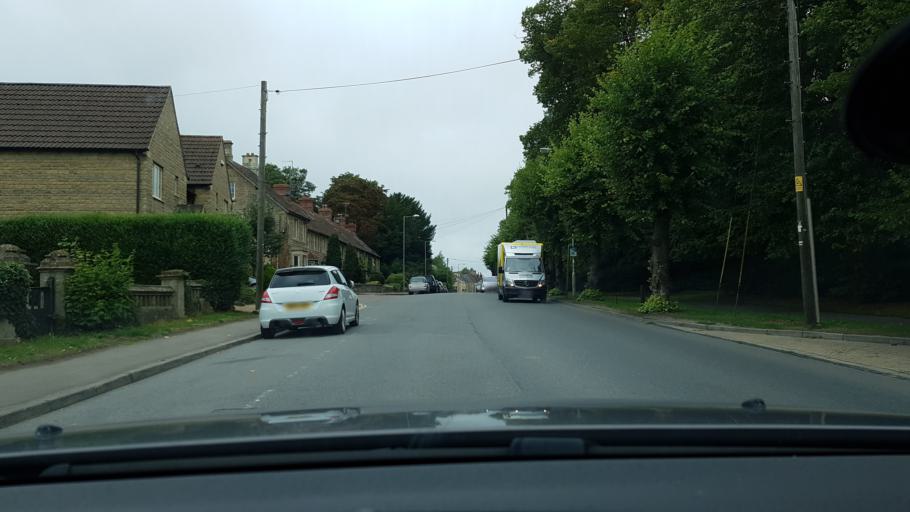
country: GB
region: England
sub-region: Wiltshire
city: Calne
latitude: 51.4297
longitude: -1.9971
